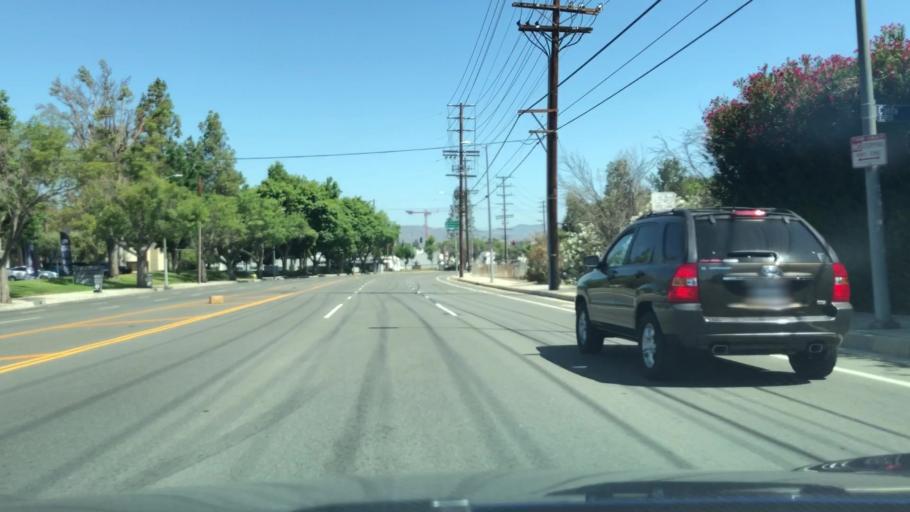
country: US
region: California
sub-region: Los Angeles County
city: Woodland Hills
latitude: 34.1777
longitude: -118.5899
